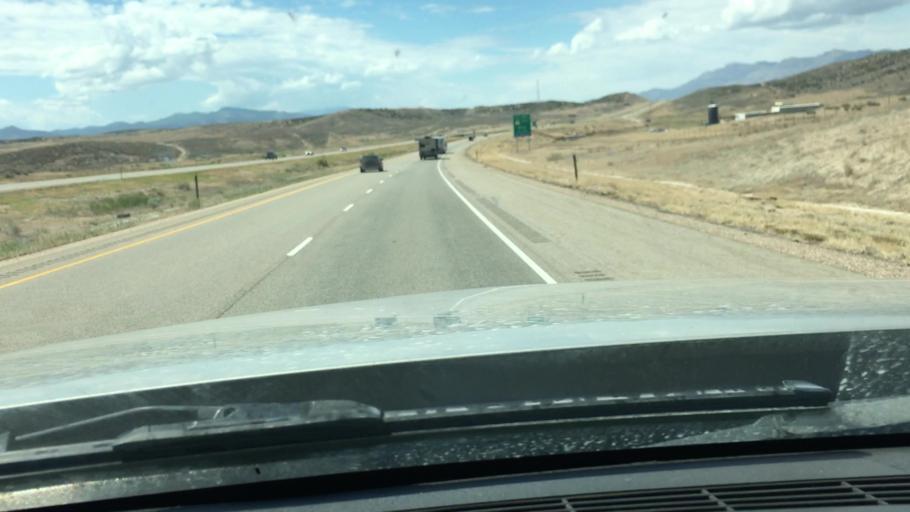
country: US
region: Utah
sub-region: Juab County
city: Nephi
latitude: 39.4939
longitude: -111.9715
